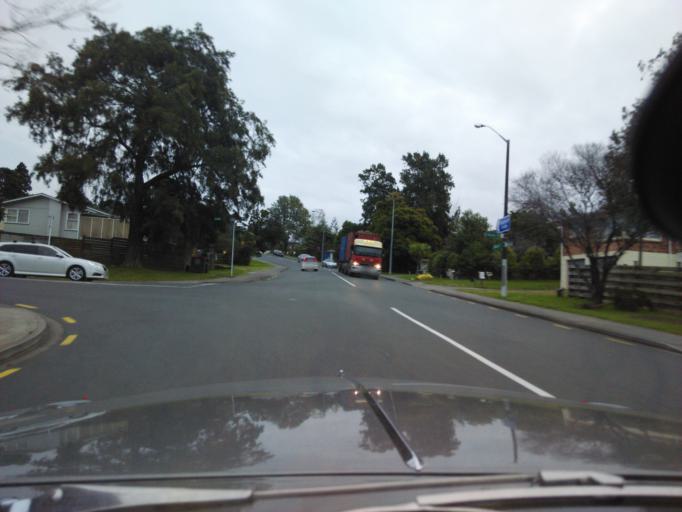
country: NZ
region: Auckland
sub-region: Auckland
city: North Shore
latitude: -36.7768
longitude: 174.7317
